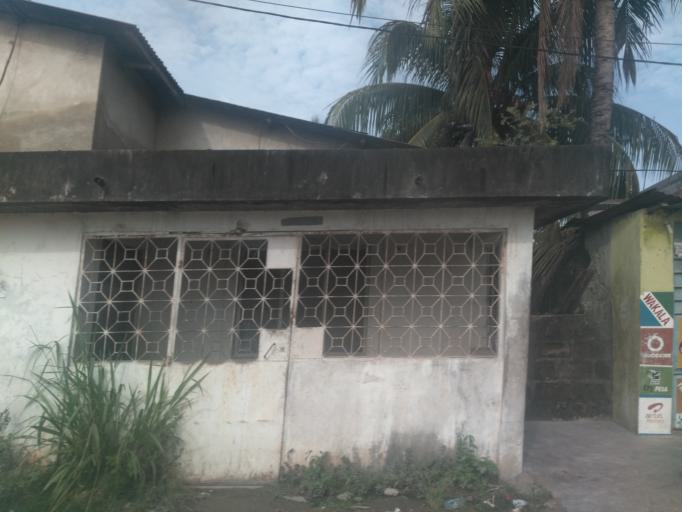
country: TZ
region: Zanzibar Urban/West
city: Zanzibar
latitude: -6.1559
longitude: 39.2088
